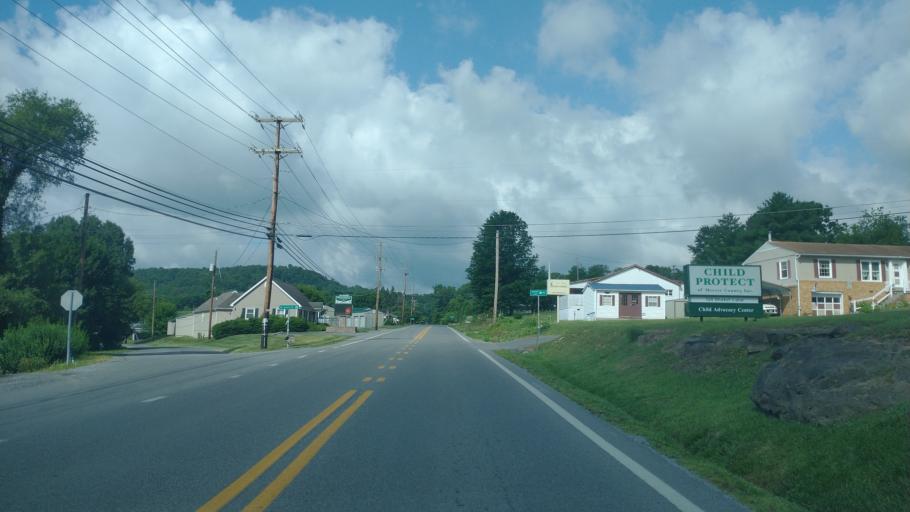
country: US
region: West Virginia
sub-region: Mercer County
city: Princeton
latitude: 37.3635
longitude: -81.1217
